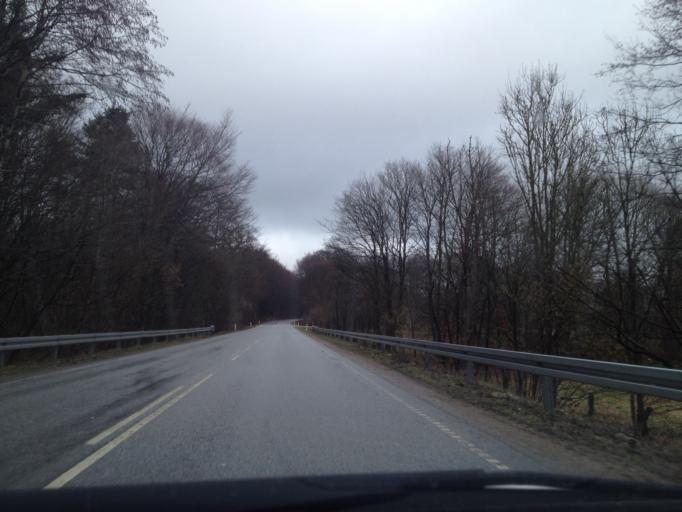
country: DK
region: South Denmark
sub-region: Kolding Kommune
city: Vamdrup
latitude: 55.3760
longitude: 9.2191
